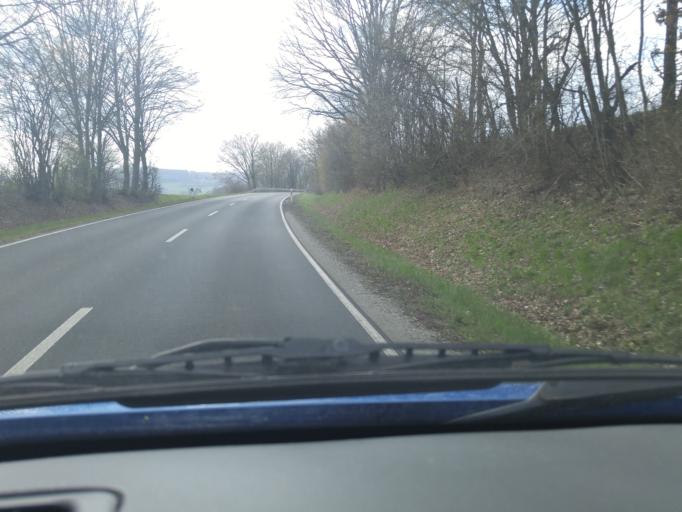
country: DE
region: Hesse
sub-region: Regierungsbezirk Kassel
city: Hosenfeld
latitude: 50.5456
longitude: 9.5088
